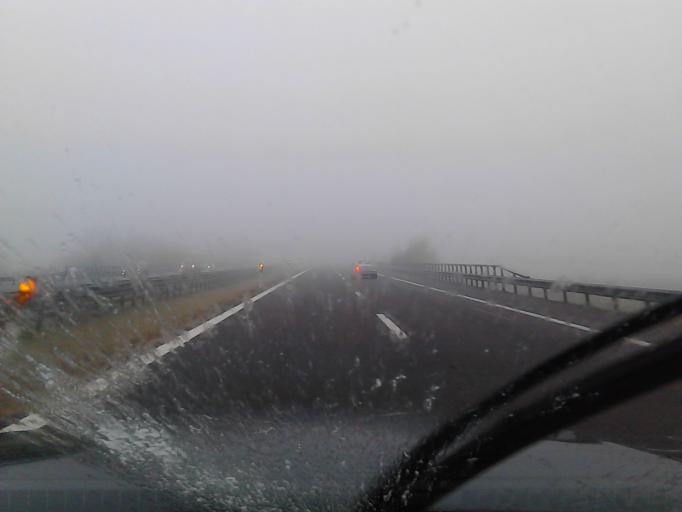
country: IT
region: Lombardy
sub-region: Provincia di Mantova
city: Castelbelforte
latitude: 45.2323
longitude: 10.8606
